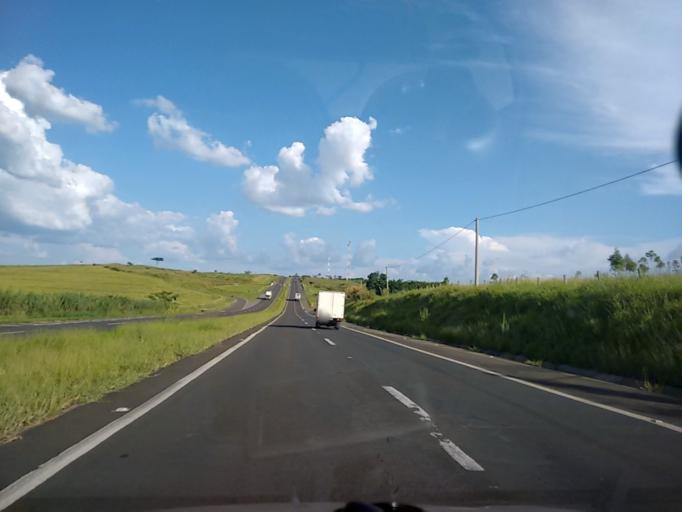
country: BR
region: Sao Paulo
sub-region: Duartina
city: Duartina
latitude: -22.2786
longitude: -49.4984
